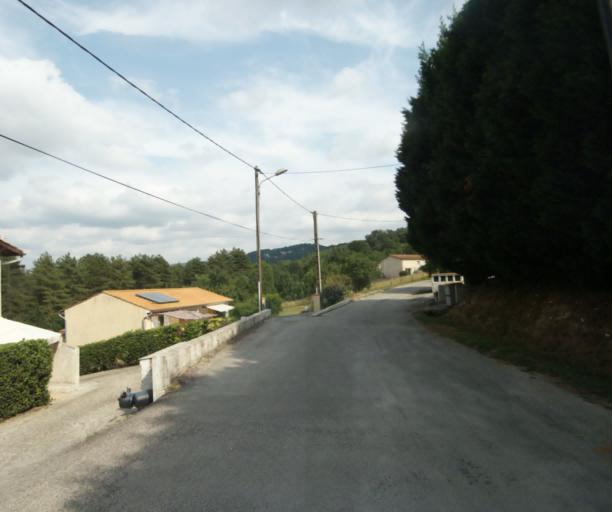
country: FR
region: Midi-Pyrenees
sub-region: Departement de la Haute-Garonne
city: Revel
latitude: 43.4409
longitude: 2.0342
